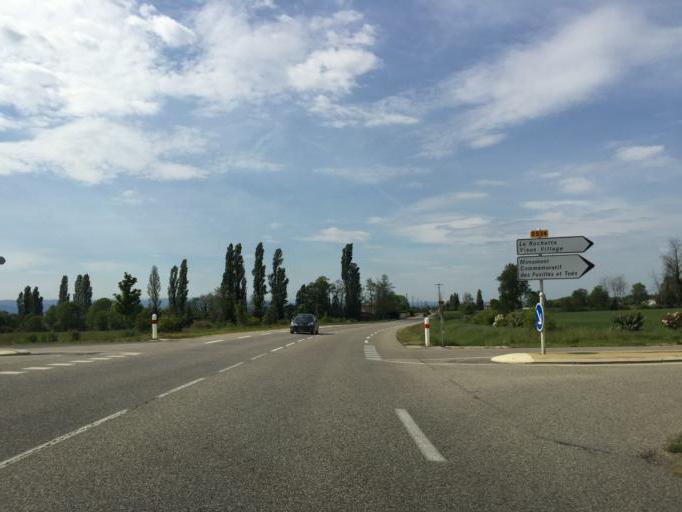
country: FR
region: Rhone-Alpes
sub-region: Departement de la Drome
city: Upie
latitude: 44.7944
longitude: 5.0195
